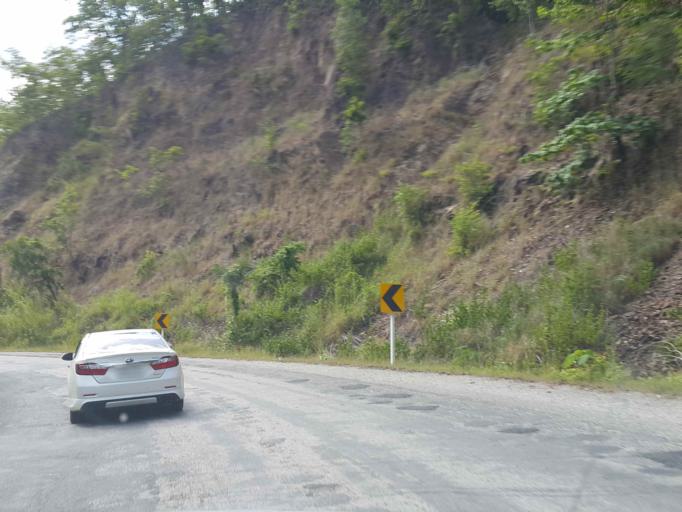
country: TH
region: Lampang
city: Thoen
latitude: 17.6390
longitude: 99.3083
